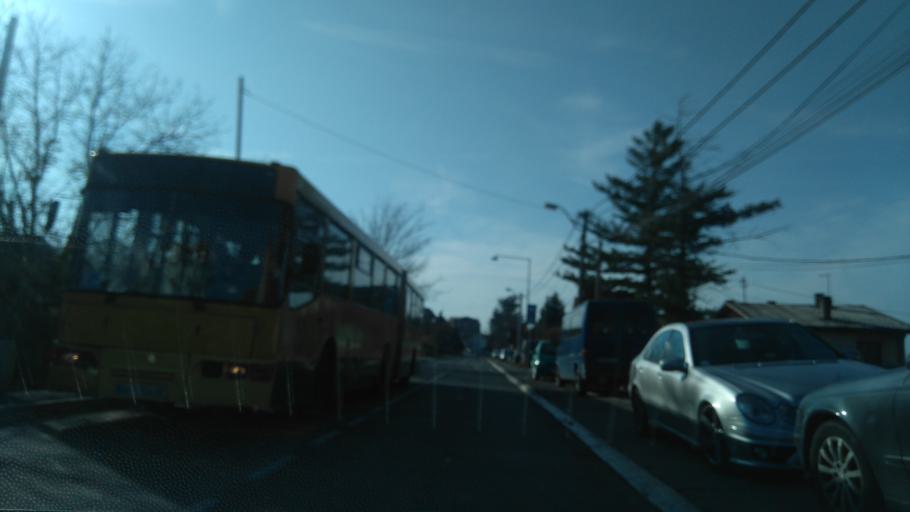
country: RS
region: Central Serbia
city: Sremcica
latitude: 44.7357
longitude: 20.3813
